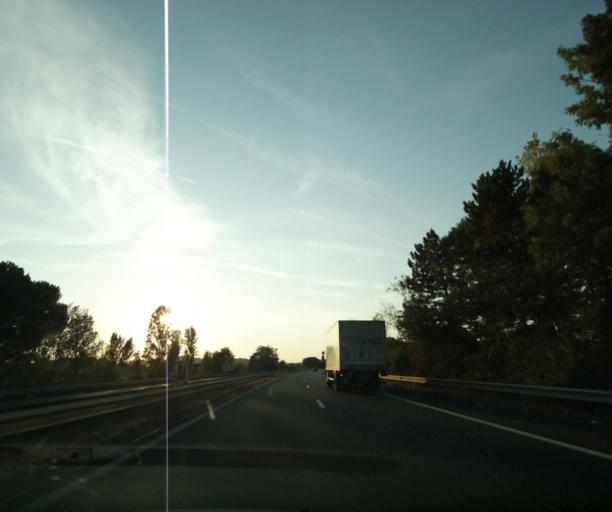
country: FR
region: Aquitaine
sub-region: Departement du Lot-et-Garonne
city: Estillac
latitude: 44.1648
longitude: 0.5894
